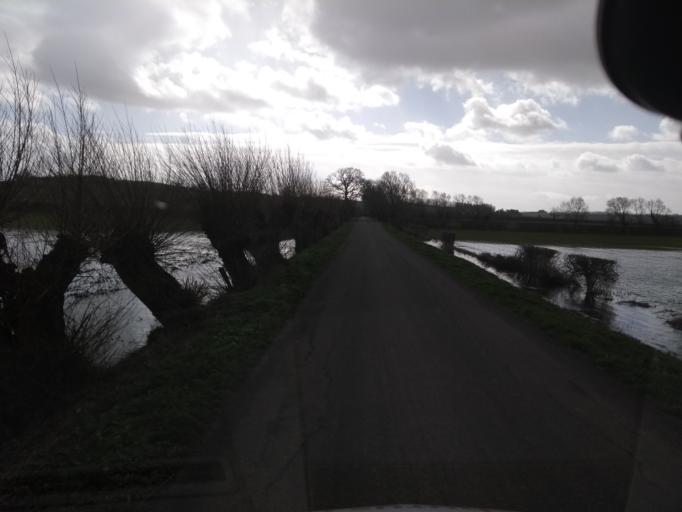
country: GB
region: England
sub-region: Somerset
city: Curry Rivel
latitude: 50.9853
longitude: -2.8499
